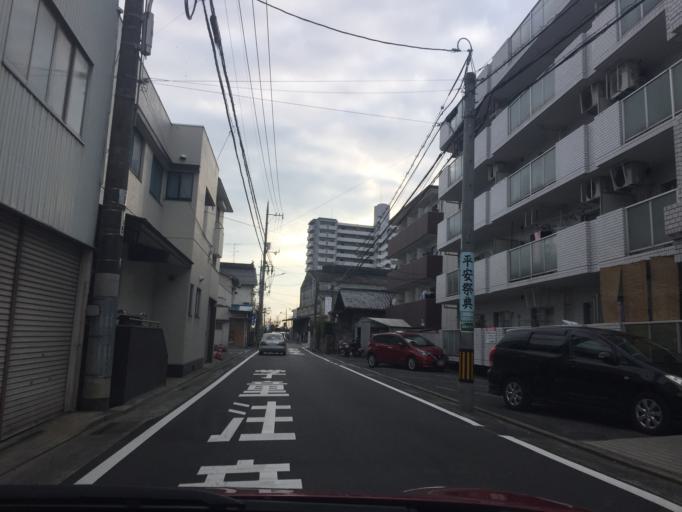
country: JP
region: Hiroshima
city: Hiroshima-shi
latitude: 34.4278
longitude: 132.4574
